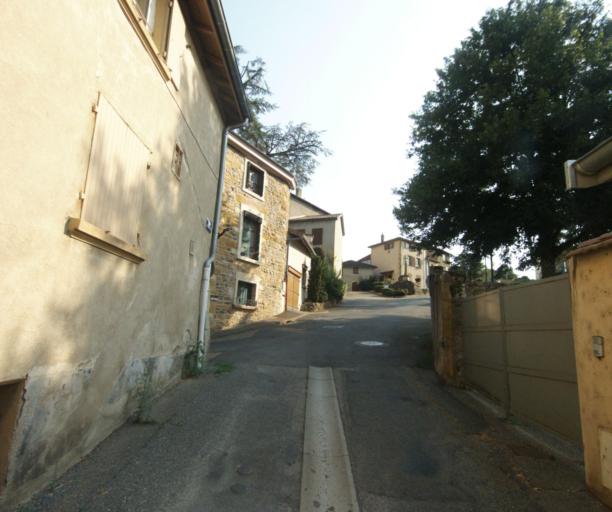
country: FR
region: Rhone-Alpes
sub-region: Departement du Rhone
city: Sain-Bel
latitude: 45.8099
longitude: 4.5973
